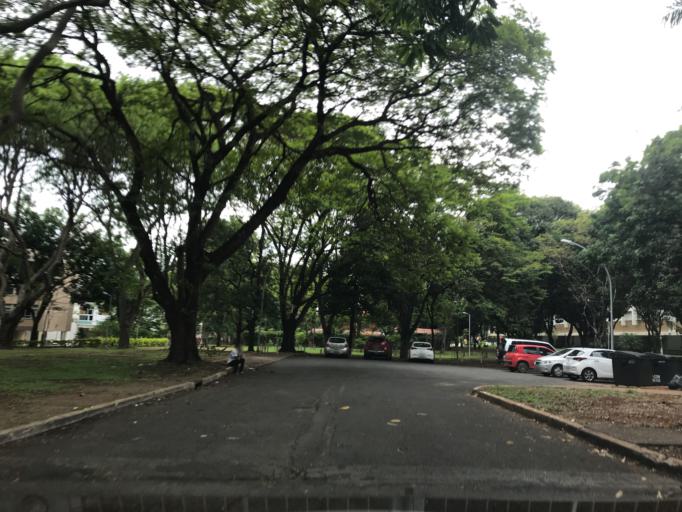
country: BR
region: Federal District
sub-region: Brasilia
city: Brasilia
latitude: -15.8116
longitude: -47.8896
